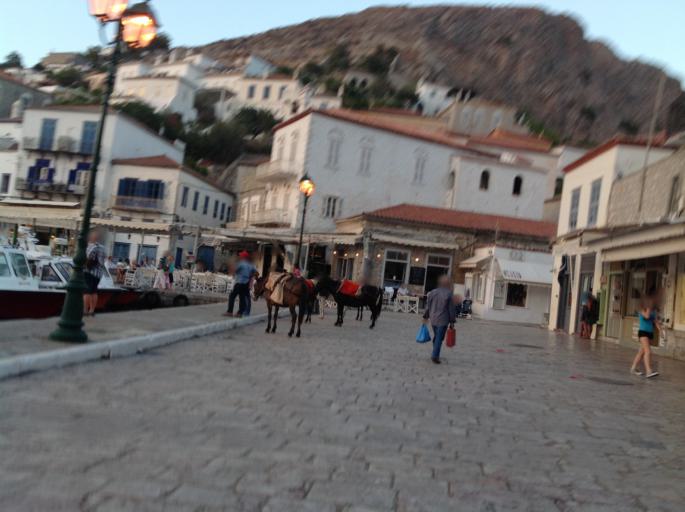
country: GR
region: Attica
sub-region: Nomos Piraios
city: Ydra
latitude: 37.3499
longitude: 23.4667
